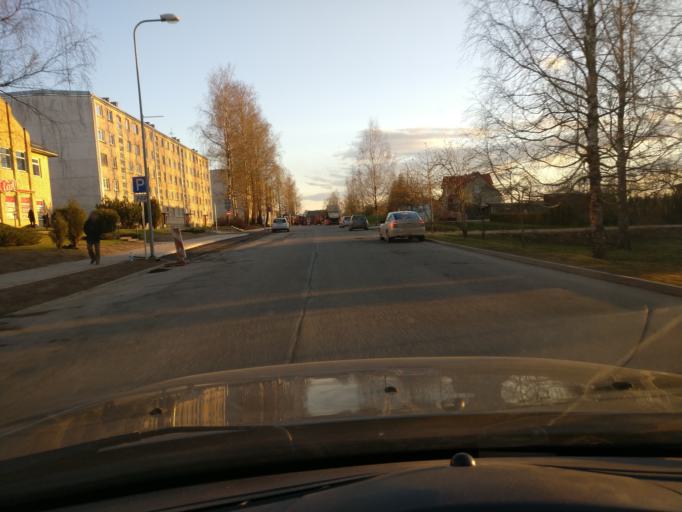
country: LV
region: Aluksnes Rajons
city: Aluksne
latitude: 57.4189
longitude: 27.0650
